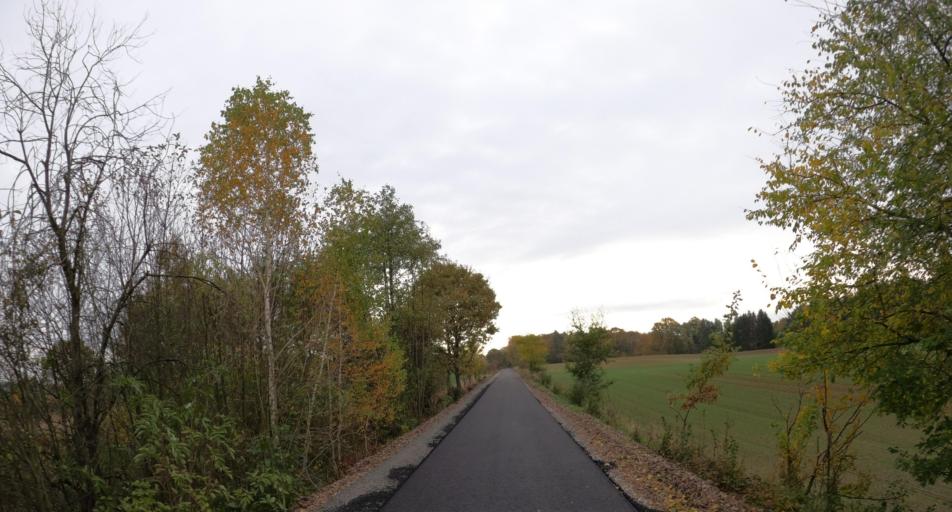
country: PL
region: West Pomeranian Voivodeship
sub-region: Powiat mysliborski
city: Nowogrodek Pomorski
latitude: 52.9870
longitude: 15.0817
